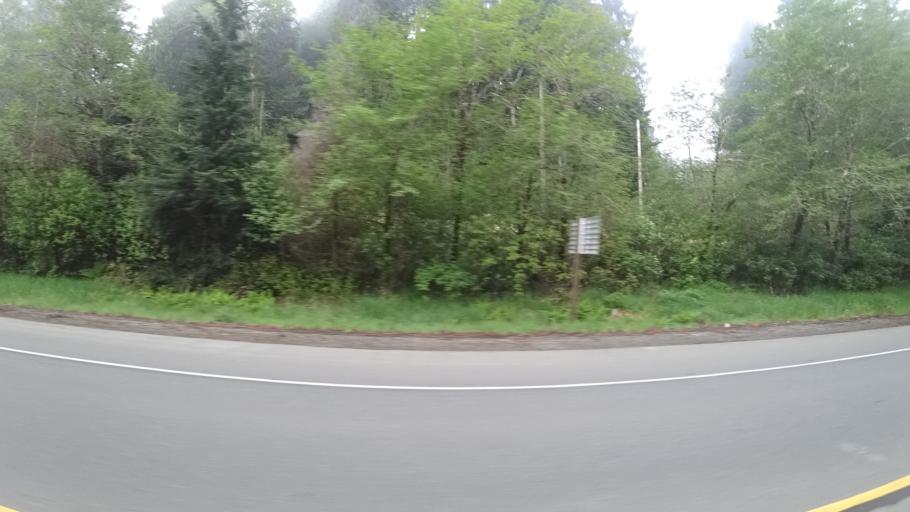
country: US
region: Oregon
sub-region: Coos County
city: Bunker Hill
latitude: 43.2909
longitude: -124.2307
